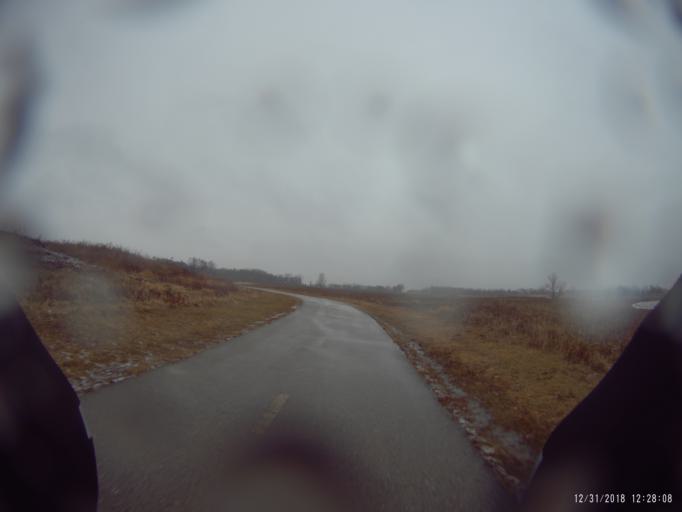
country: US
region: Wisconsin
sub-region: Dane County
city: Verona
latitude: 42.9962
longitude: -89.5171
